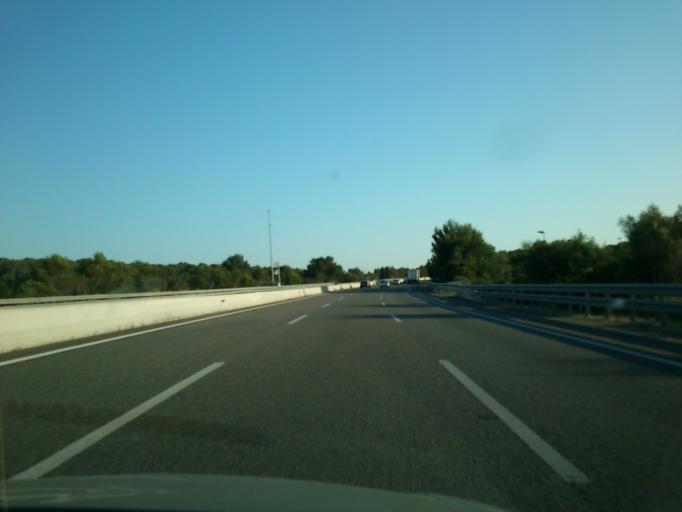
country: ES
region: Catalonia
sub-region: Provincia de Tarragona
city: El Vendrell
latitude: 41.2040
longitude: 1.5086
